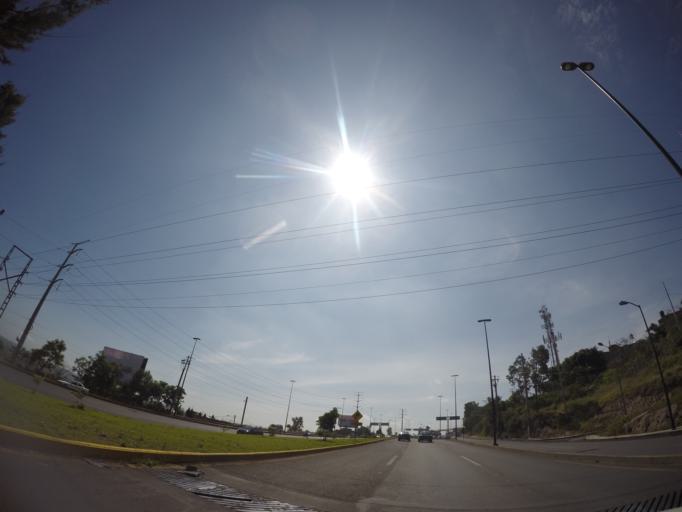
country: MX
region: Michoacan
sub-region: Tarimbaro
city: Real Hacienda (Metropolis)
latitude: 19.7244
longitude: -101.1963
